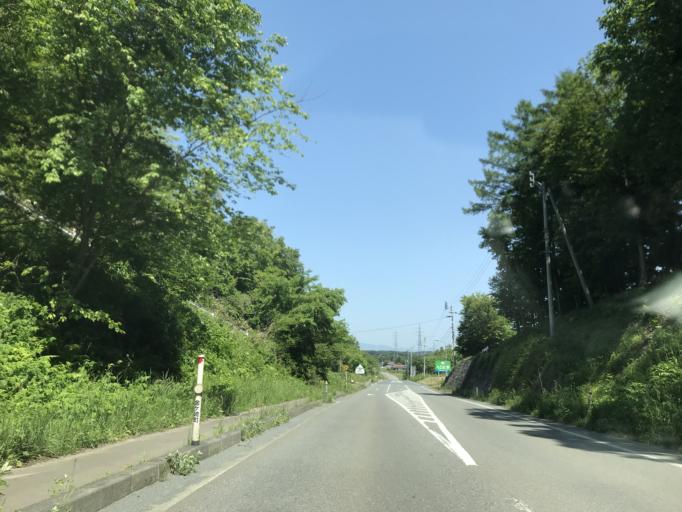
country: JP
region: Iwate
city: Mizusawa
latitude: 39.1725
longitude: 141.0829
